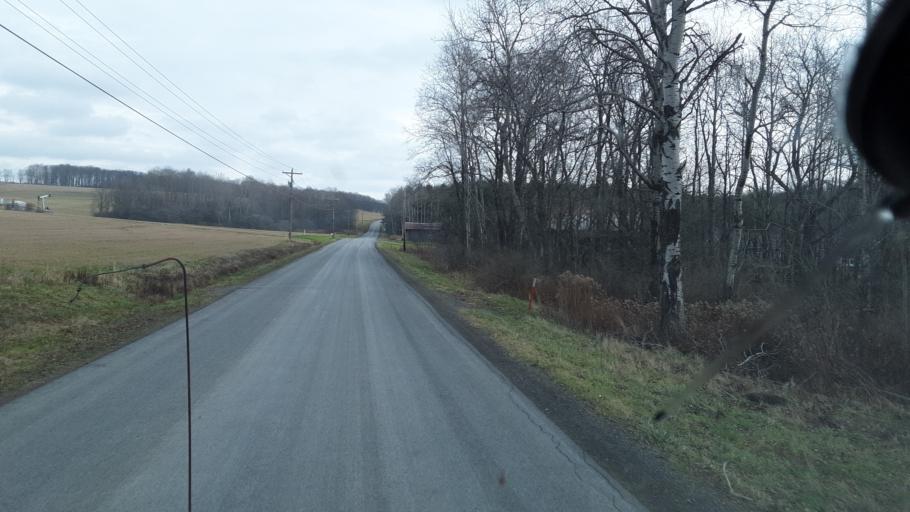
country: US
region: Pennsylvania
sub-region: Potter County
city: Galeton
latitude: 41.8877
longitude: -77.7772
